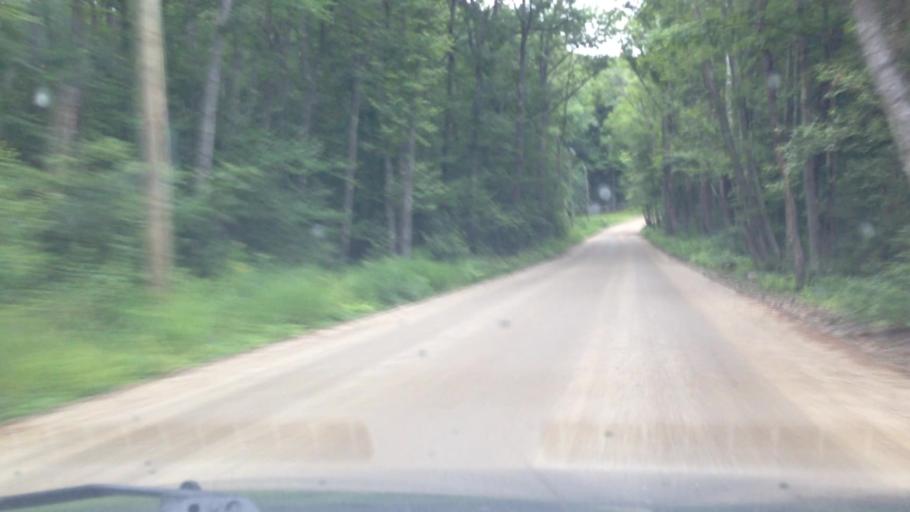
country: US
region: New Hampshire
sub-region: Cheshire County
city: Marlborough
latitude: 42.8949
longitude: -72.1624
